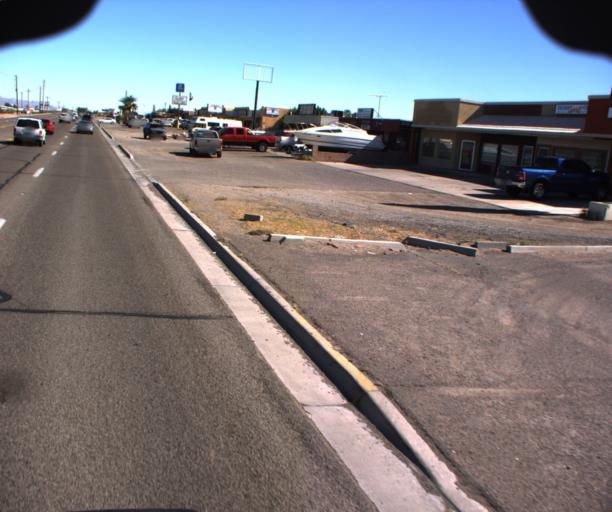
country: US
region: Arizona
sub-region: Mohave County
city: Mohave Valley
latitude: 35.0302
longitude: -114.5979
